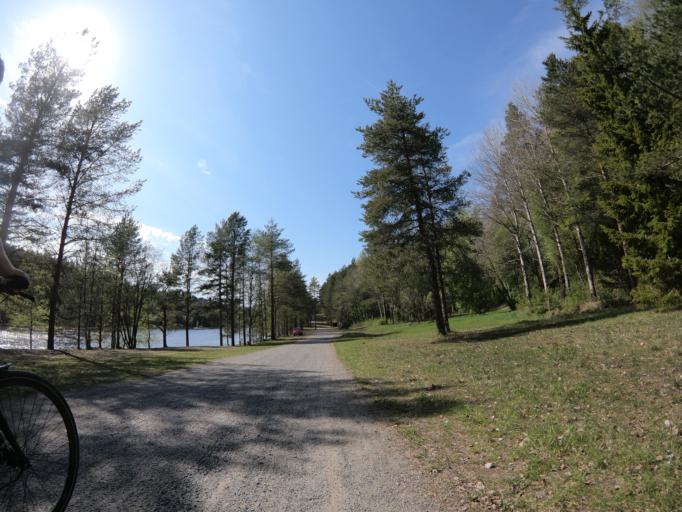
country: SE
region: Vaesterbotten
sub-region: Umea Kommun
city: Roback
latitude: 63.8295
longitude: 20.1701
